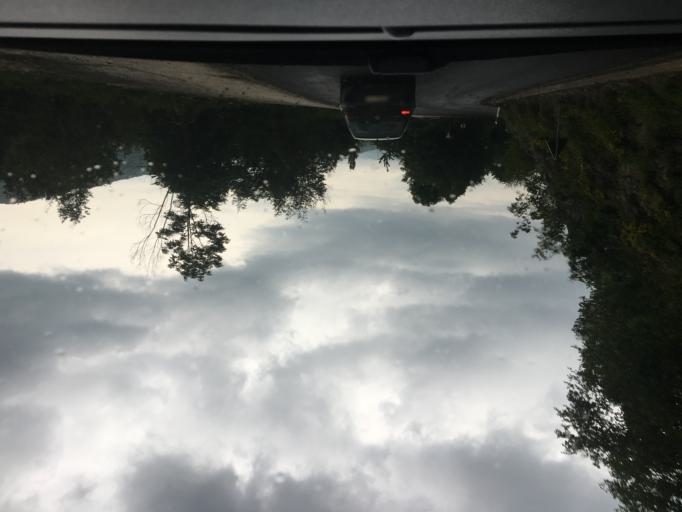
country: MK
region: Gostivar
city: Vrutok
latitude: 41.6826
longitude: 20.8490
